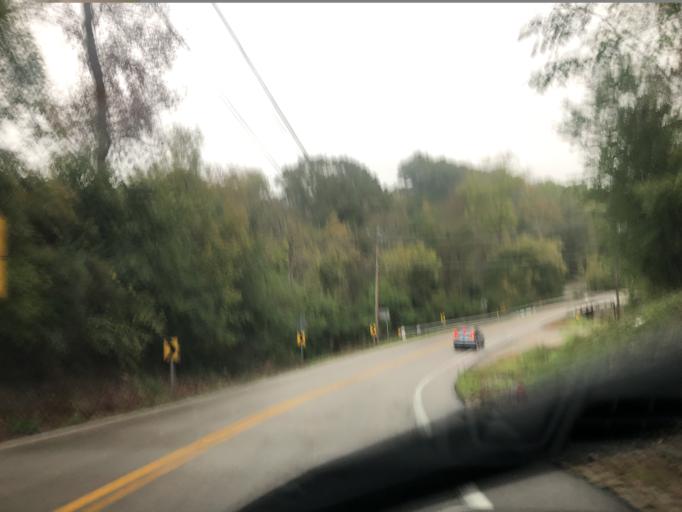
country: US
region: Ohio
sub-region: Clermont County
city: Mulberry
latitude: 39.2046
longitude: -84.2493
